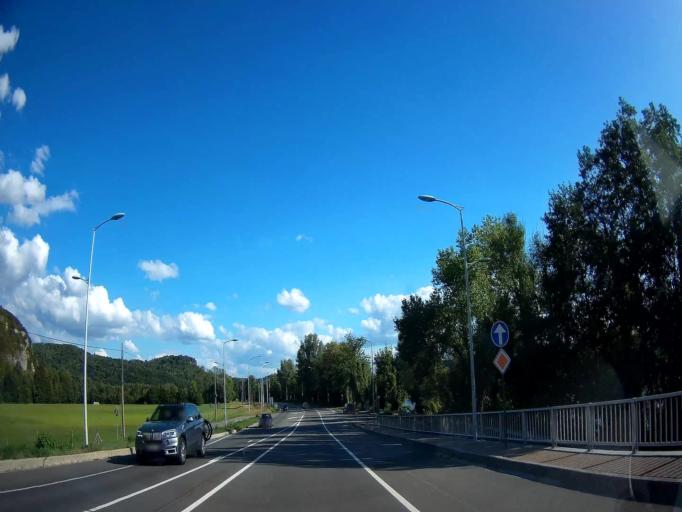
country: BE
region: Wallonia
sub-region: Province de Namur
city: Anhee
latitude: 50.3147
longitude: 4.8792
